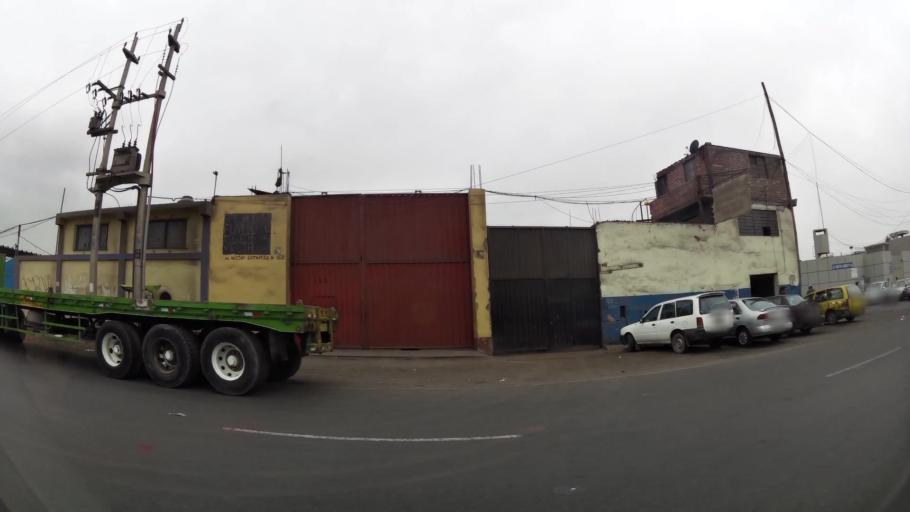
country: PE
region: Callao
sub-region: Callao
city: Callao
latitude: -12.0471
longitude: -77.1263
